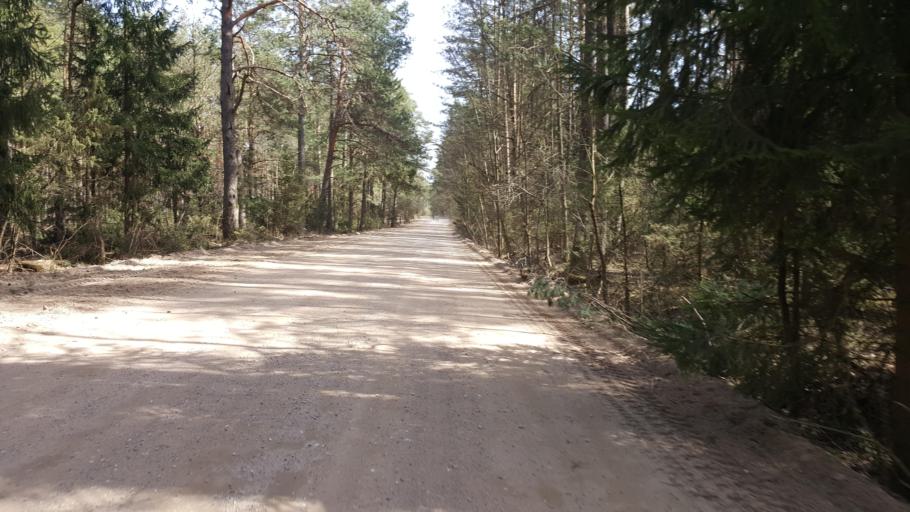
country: BY
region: Brest
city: Kamyanyuki
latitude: 52.5625
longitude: 23.7831
